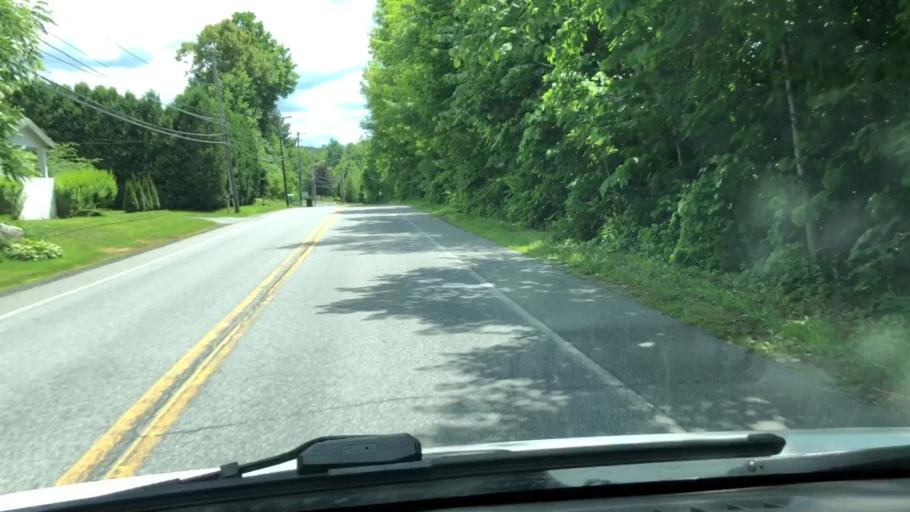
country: US
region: Massachusetts
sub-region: Berkshire County
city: Adams
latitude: 42.5980
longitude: -73.1180
